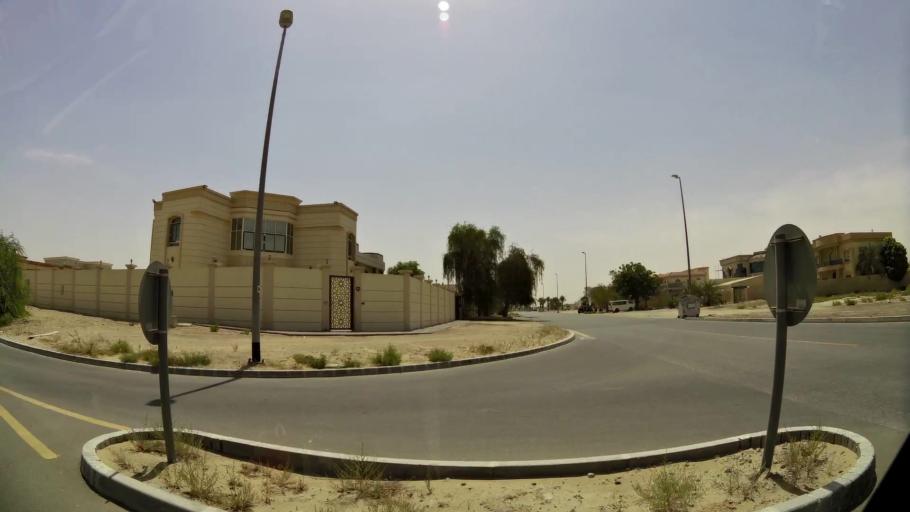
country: AE
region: Ash Shariqah
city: Sharjah
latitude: 25.1797
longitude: 55.4222
